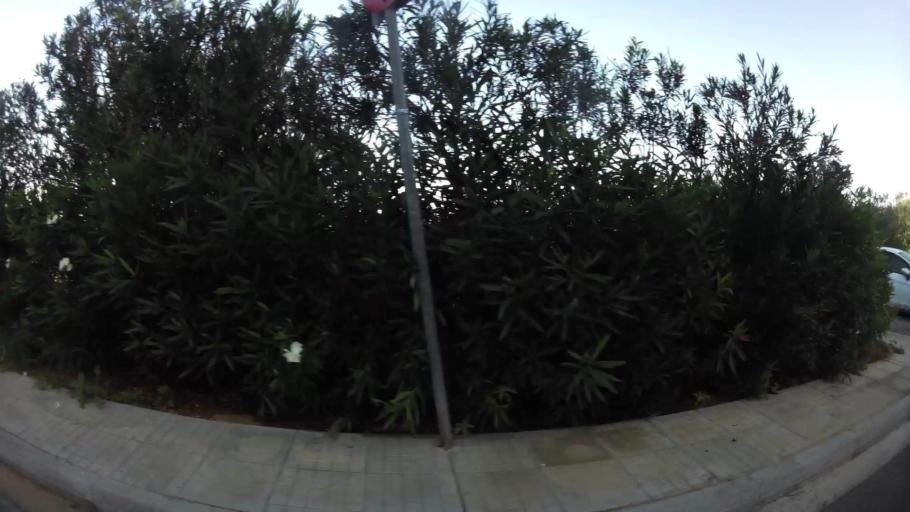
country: GR
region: Attica
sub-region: Nomarchia Anatolikis Attikis
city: Pallini
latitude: 38.0085
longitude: 23.8779
